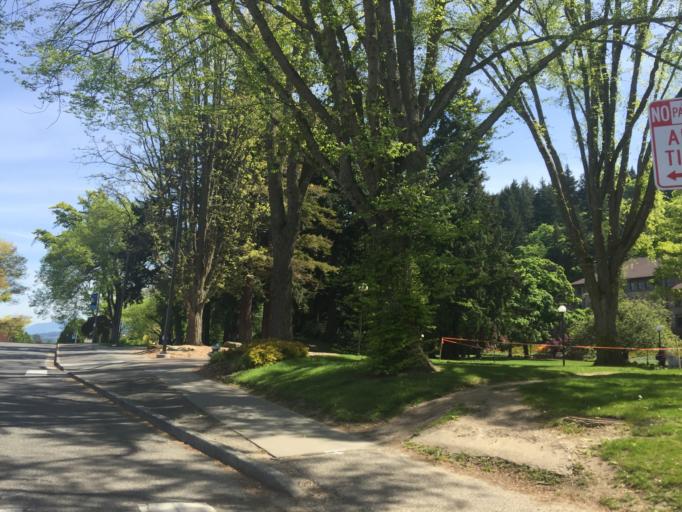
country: US
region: Washington
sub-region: Whatcom County
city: Bellingham
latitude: 48.7382
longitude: -122.4861
